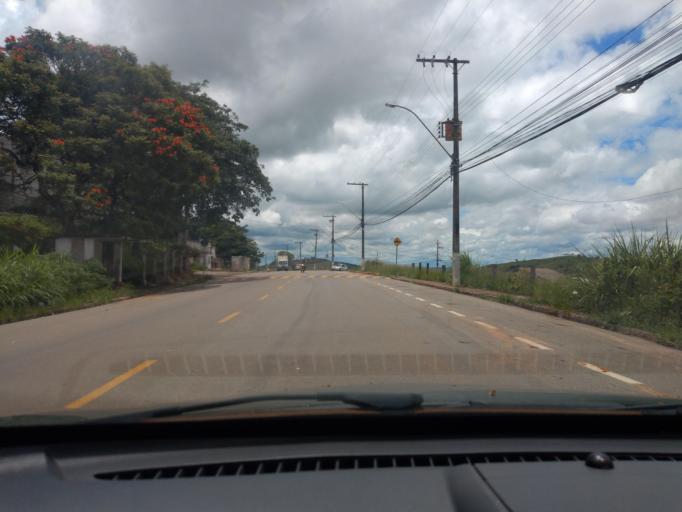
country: BR
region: Minas Gerais
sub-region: Lavras
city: Lavras
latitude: -21.2410
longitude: -45.0225
